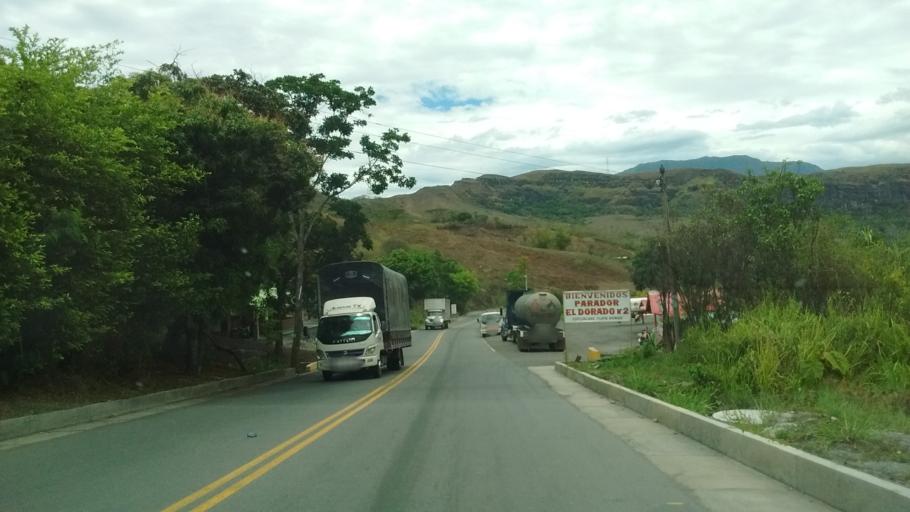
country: CO
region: Cauca
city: La Sierra
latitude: 2.2006
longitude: -76.8163
